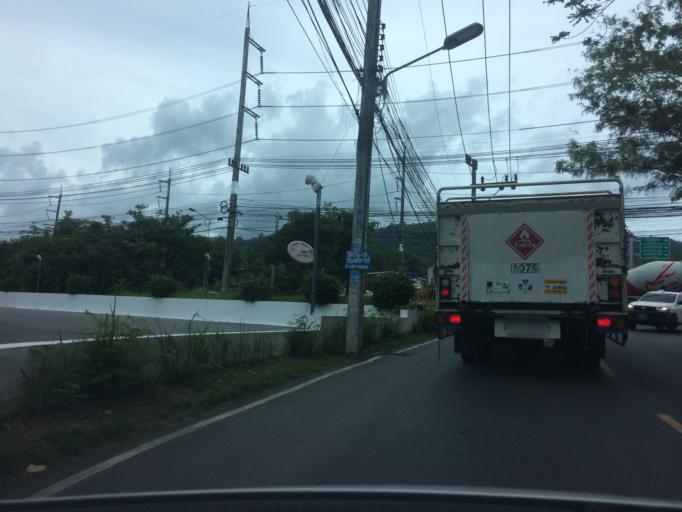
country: TH
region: Phuket
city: Mueang Phuket
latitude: 7.8671
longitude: 98.3559
